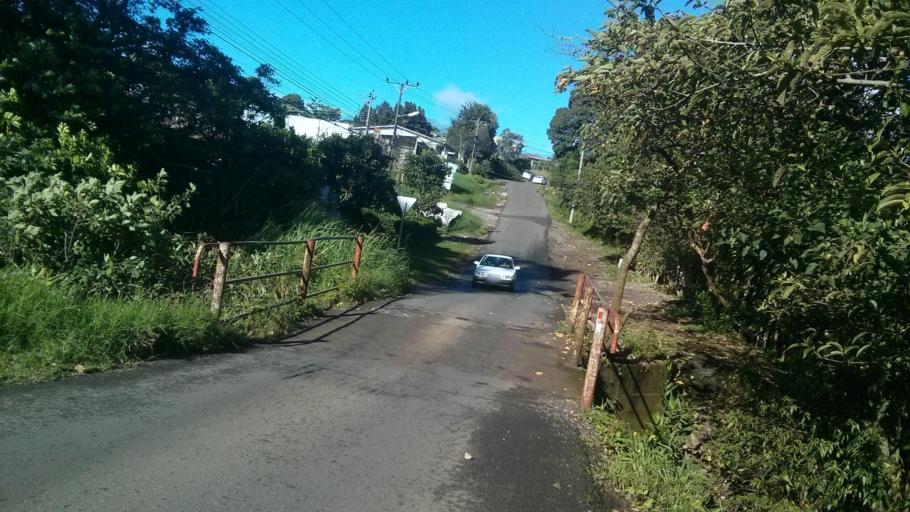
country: CR
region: Heredia
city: Angeles
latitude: 10.0137
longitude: -84.0474
